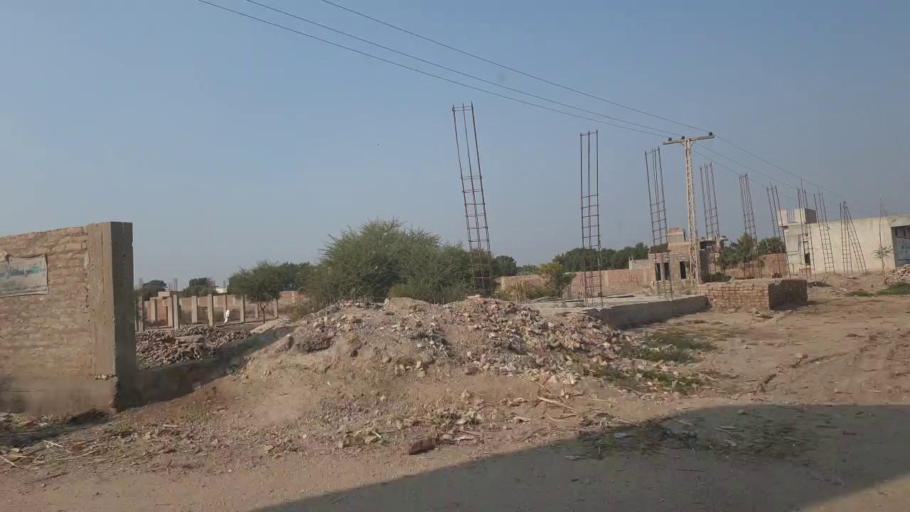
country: PK
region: Sindh
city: Tando Allahyar
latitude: 25.4346
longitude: 68.7083
